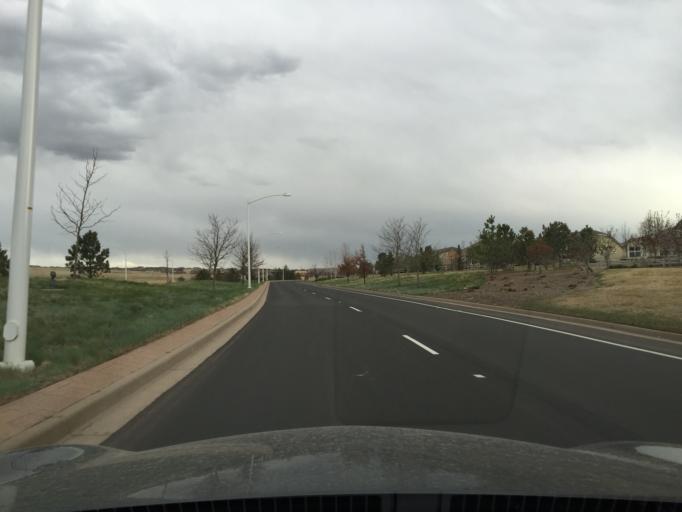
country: US
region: Colorado
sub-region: Boulder County
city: Lafayette
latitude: 39.9951
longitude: -105.0388
